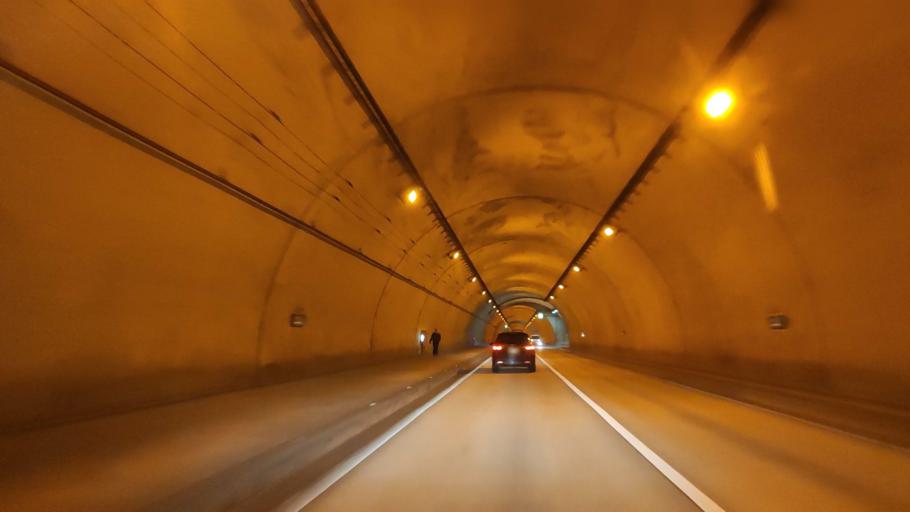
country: JP
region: Ehime
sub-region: Shikoku-chuo Shi
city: Matsuyama
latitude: 33.8800
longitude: 132.7118
